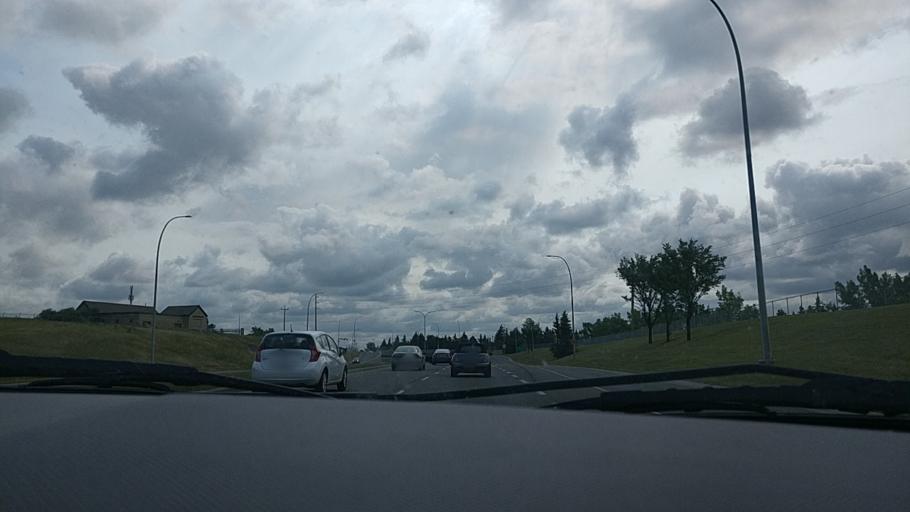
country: CA
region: Alberta
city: Calgary
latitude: 51.0907
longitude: -114.0994
